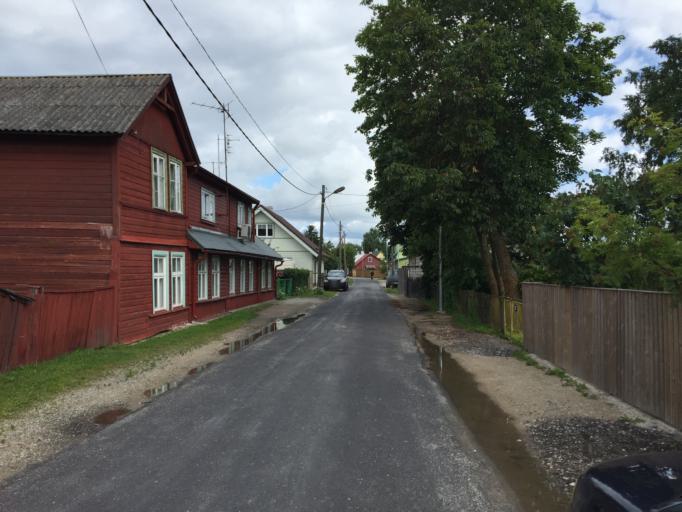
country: EE
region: Laeaene
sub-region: Haapsalu linn
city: Haapsalu
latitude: 58.9417
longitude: 23.5373
